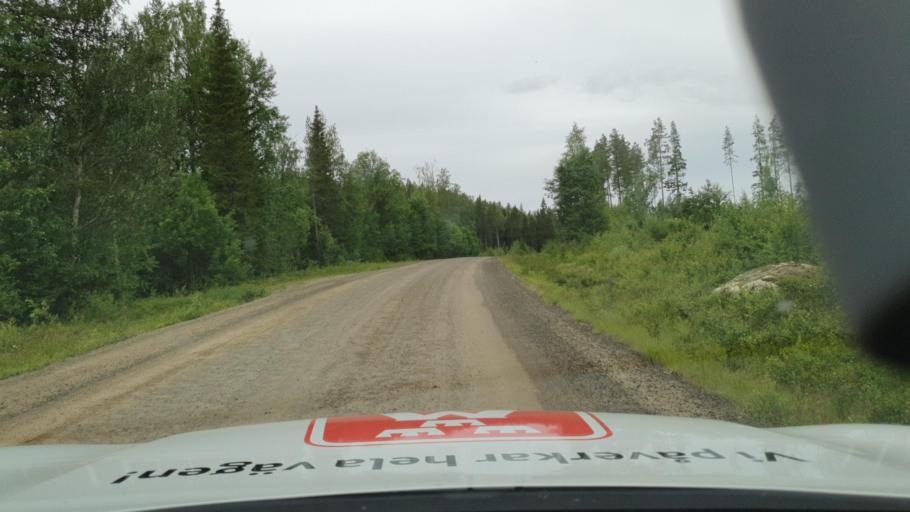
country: SE
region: Vaesterbotten
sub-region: Skelleftea Kommun
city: Burtraesk
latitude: 64.3158
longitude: 20.6464
